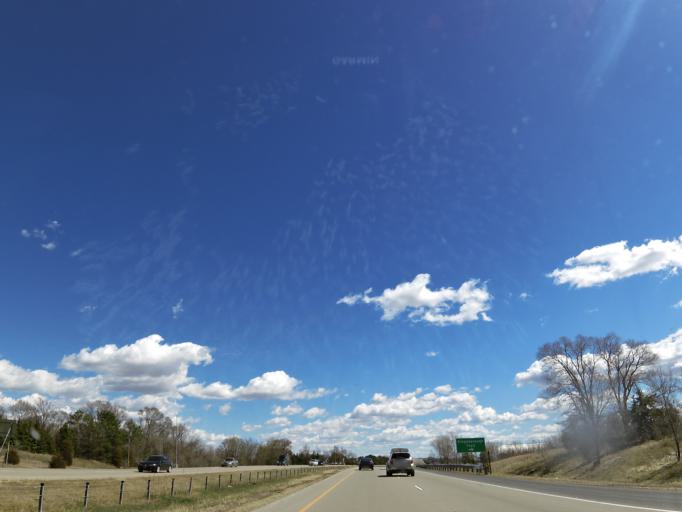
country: US
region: Minnesota
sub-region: Washington County
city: Cottage Grove
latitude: 44.7949
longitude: -92.8916
